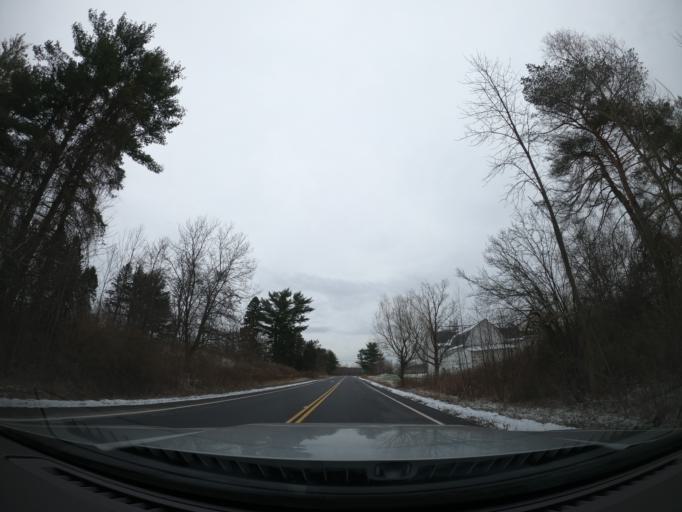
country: US
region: New York
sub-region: Tompkins County
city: Northeast Ithaca
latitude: 42.4822
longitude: -76.4520
